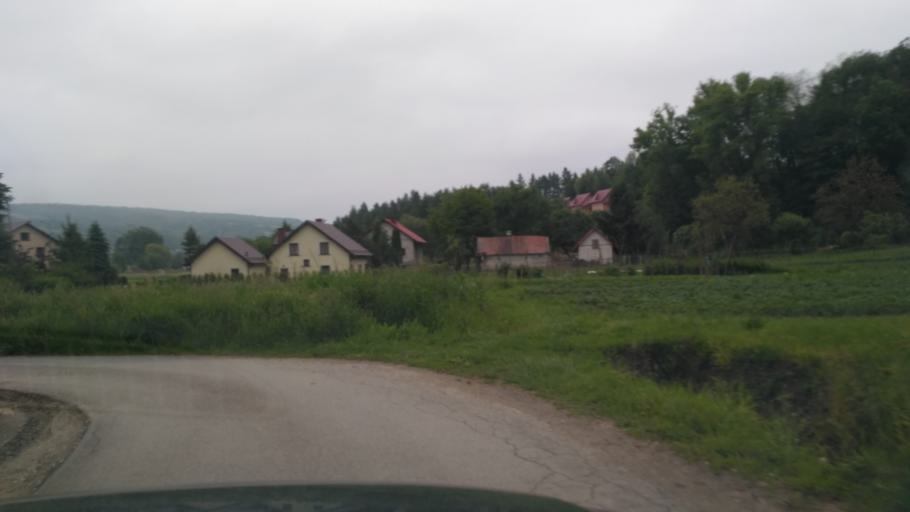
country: PL
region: Subcarpathian Voivodeship
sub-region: Powiat rzeszowski
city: Dynow
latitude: 49.8107
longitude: 22.2361
